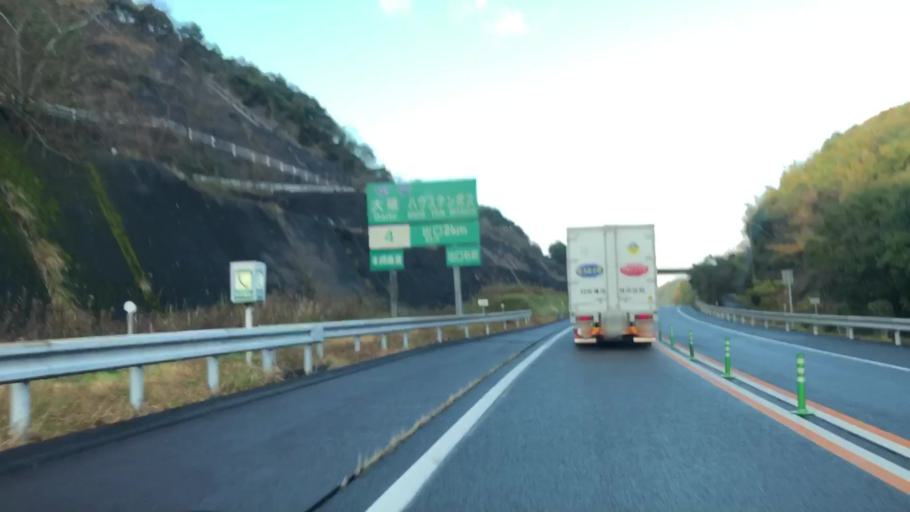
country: JP
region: Nagasaki
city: Sasebo
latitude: 33.1503
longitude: 129.8045
